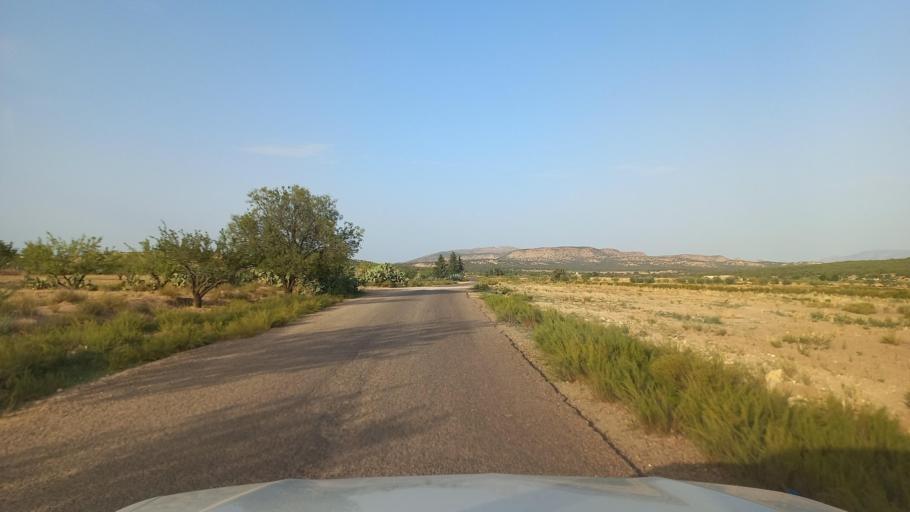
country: TN
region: Al Qasrayn
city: Sbiba
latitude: 35.4033
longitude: 8.8985
